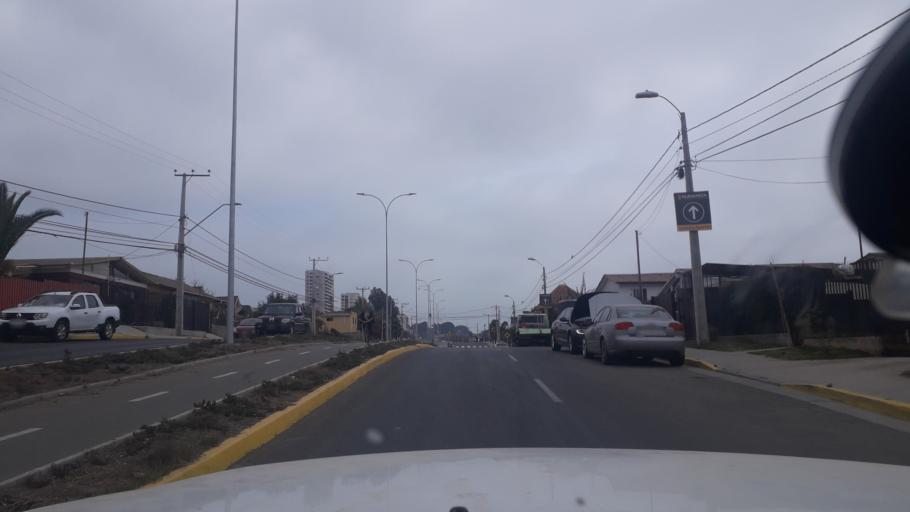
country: CL
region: Valparaiso
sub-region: Provincia de Valparaiso
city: Vina del Mar
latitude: -32.9353
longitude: -71.5285
